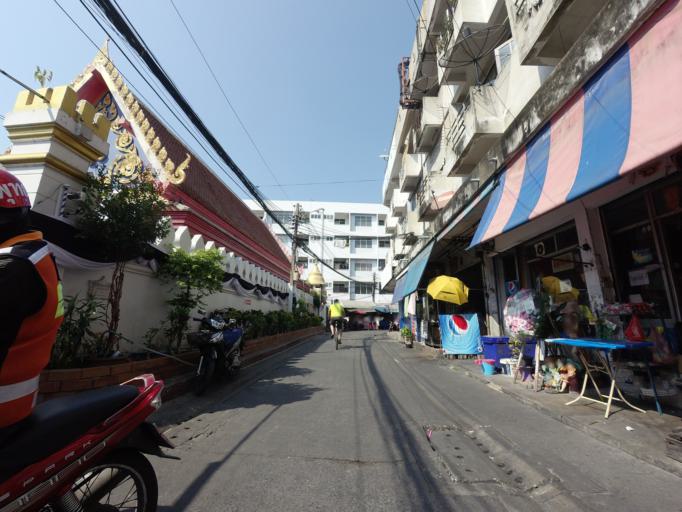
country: TH
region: Bangkok
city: Khlong Toei
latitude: 13.7081
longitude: 100.5638
